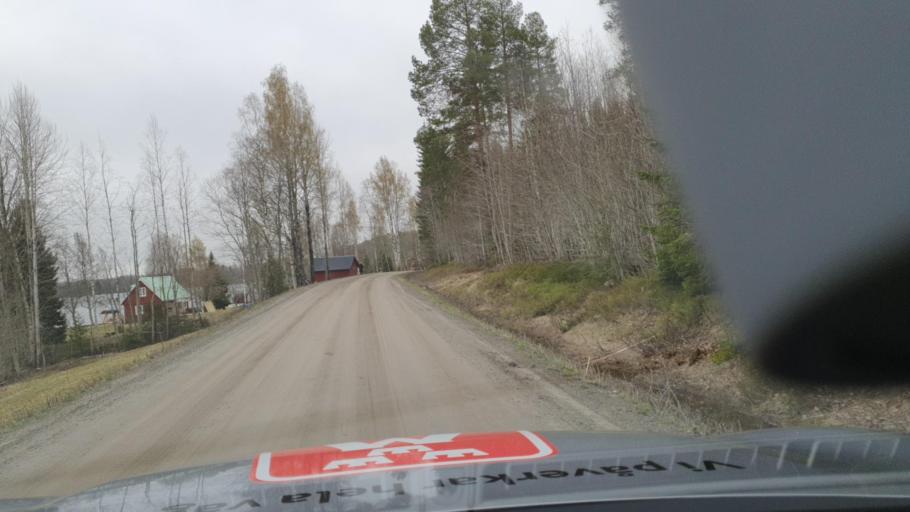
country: SE
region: Vaesternorrland
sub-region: OErnskoeldsviks Kommun
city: Husum
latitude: 63.6405
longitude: 19.0582
